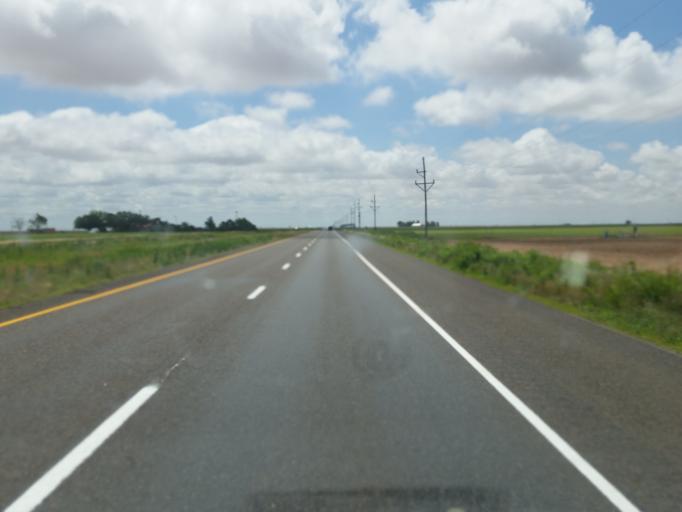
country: US
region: Texas
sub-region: Lubbock County
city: Slaton
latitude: 33.4006
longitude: -101.6136
